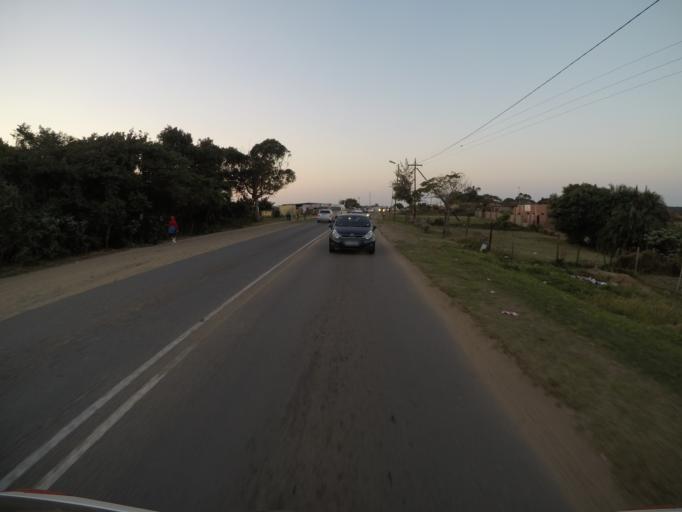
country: ZA
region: KwaZulu-Natal
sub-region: uThungulu District Municipality
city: Richards Bay
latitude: -28.7597
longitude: 32.1328
